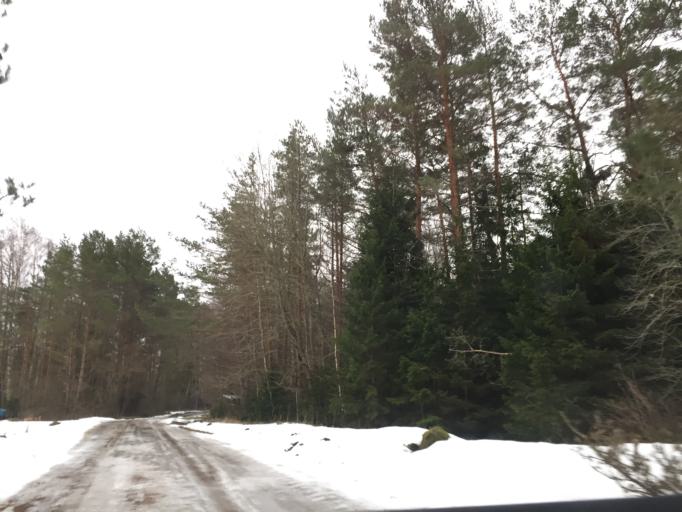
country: EE
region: Saare
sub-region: Kuressaare linn
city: Kuressaare
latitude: 58.4786
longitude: 22.2516
